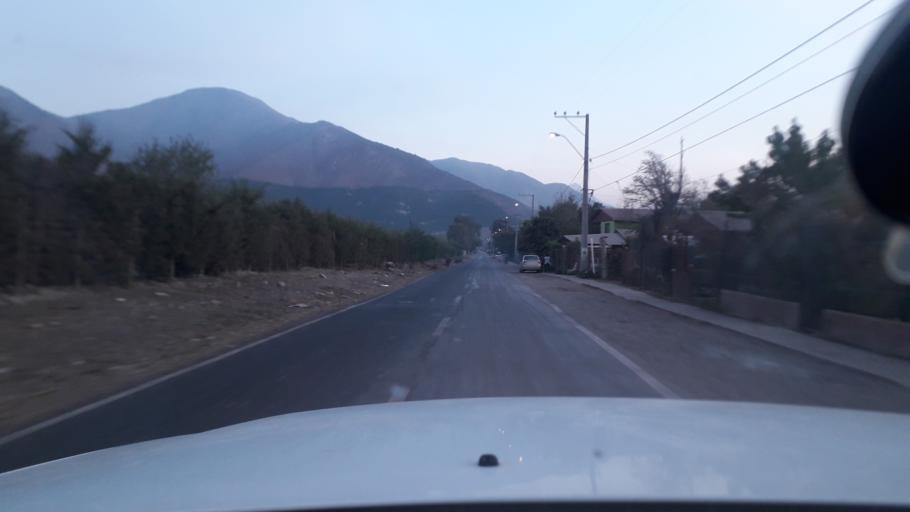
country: CL
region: Valparaiso
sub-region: Provincia de San Felipe
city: Llaillay
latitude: -32.8230
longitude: -71.0288
